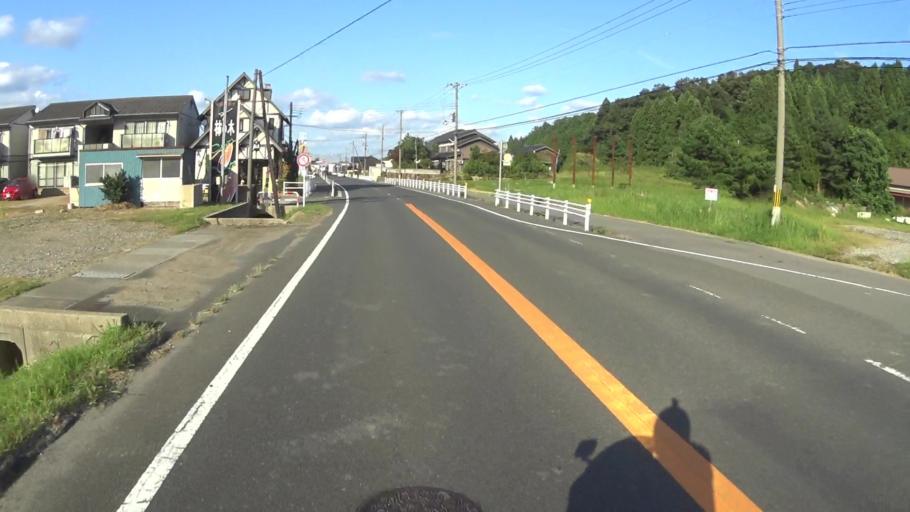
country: JP
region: Hyogo
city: Toyooka
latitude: 35.5986
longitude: 134.8904
